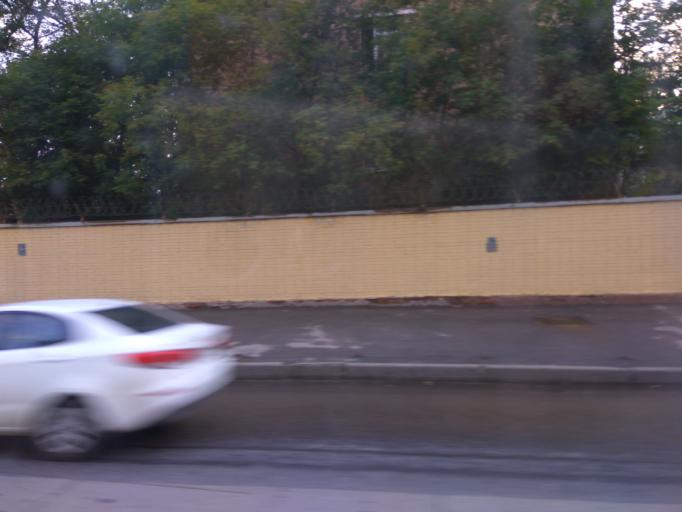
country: RU
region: Moskovskaya
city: Bogorodskoye
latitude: 55.8053
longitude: 37.7071
